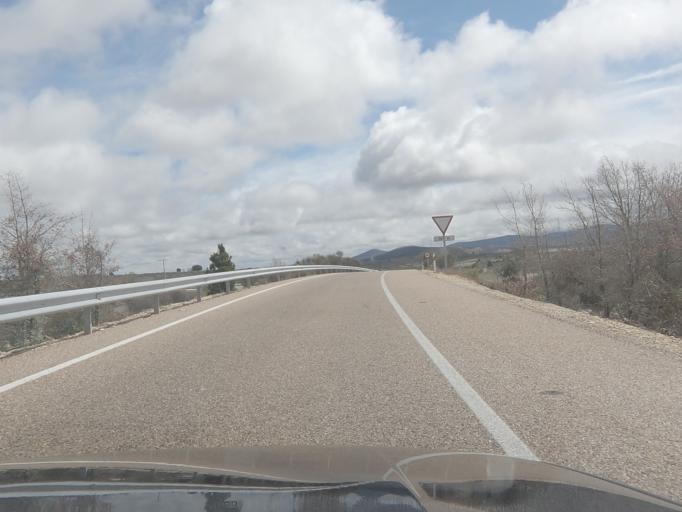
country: ES
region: Castille and Leon
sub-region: Provincia de Zamora
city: Villardeciervos
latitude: 42.0048
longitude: -6.2552
